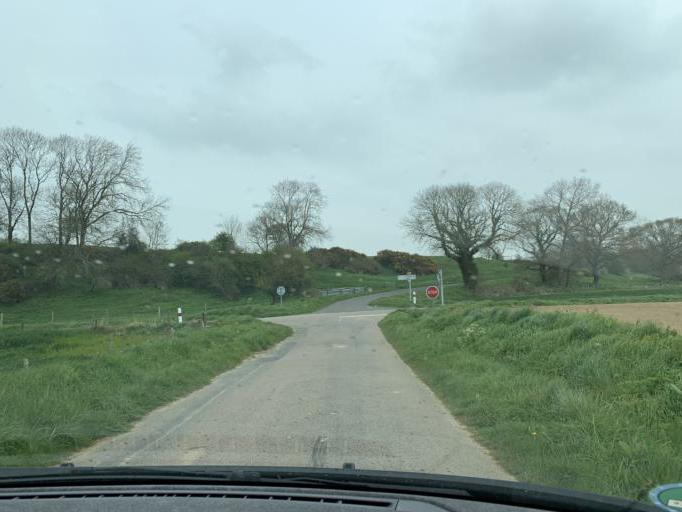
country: FR
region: Haute-Normandie
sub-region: Departement de la Seine-Maritime
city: Fontaine-le-Dun
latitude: 49.8567
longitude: 0.8184
